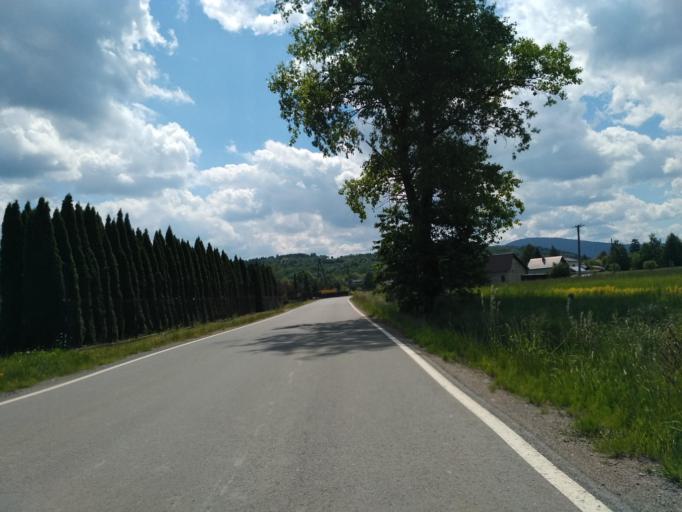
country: PL
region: Subcarpathian Voivodeship
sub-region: Powiat krosnienski
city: Dukla
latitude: 49.5796
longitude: 21.6951
